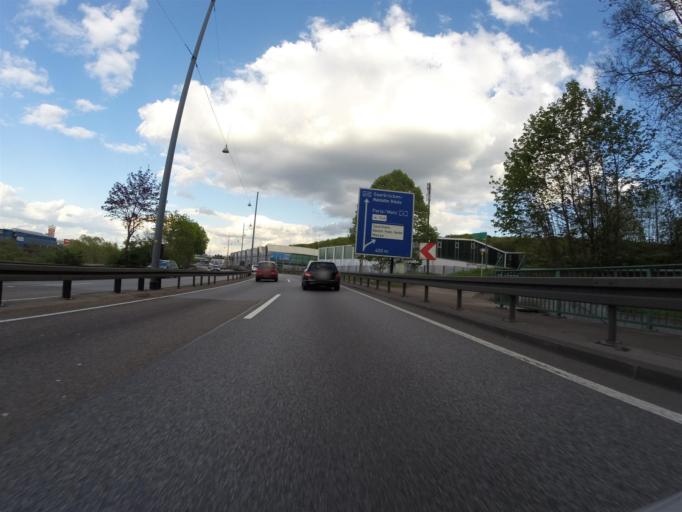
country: DE
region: Saarland
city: Saarbrucken
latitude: 49.2333
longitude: 6.9528
